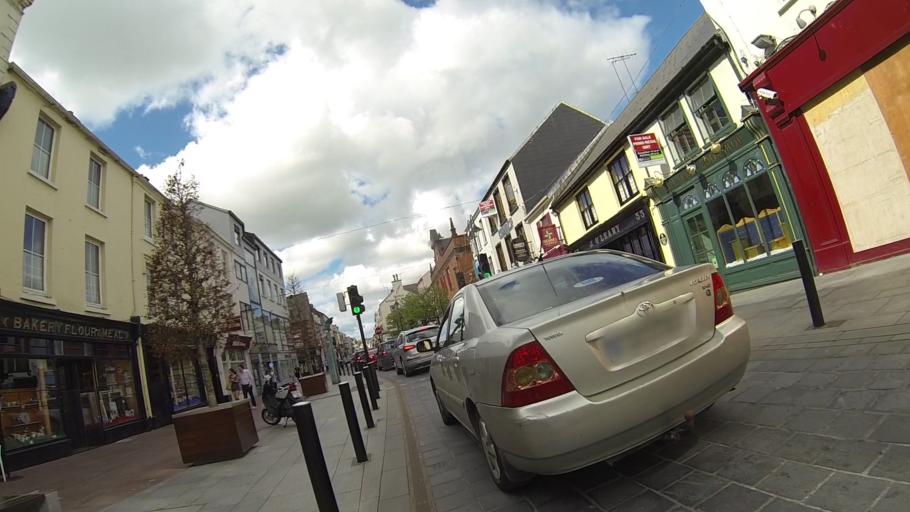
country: IE
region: Munster
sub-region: Ciarrai
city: Cill Airne
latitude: 52.0588
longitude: -9.5092
